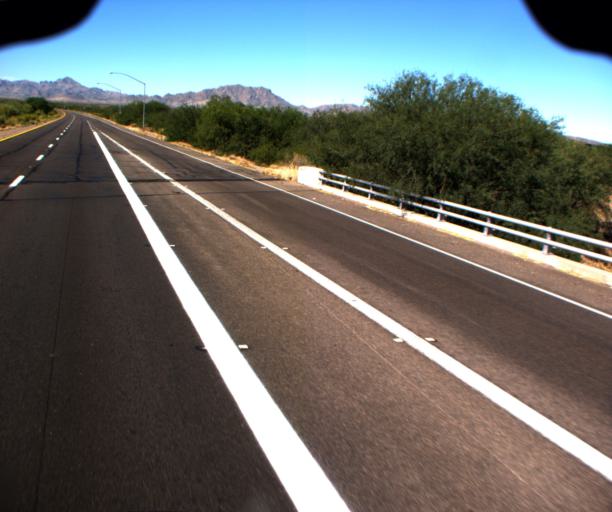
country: US
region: Arizona
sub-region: Pima County
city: Arivaca Junction
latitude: 31.7223
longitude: -111.0604
